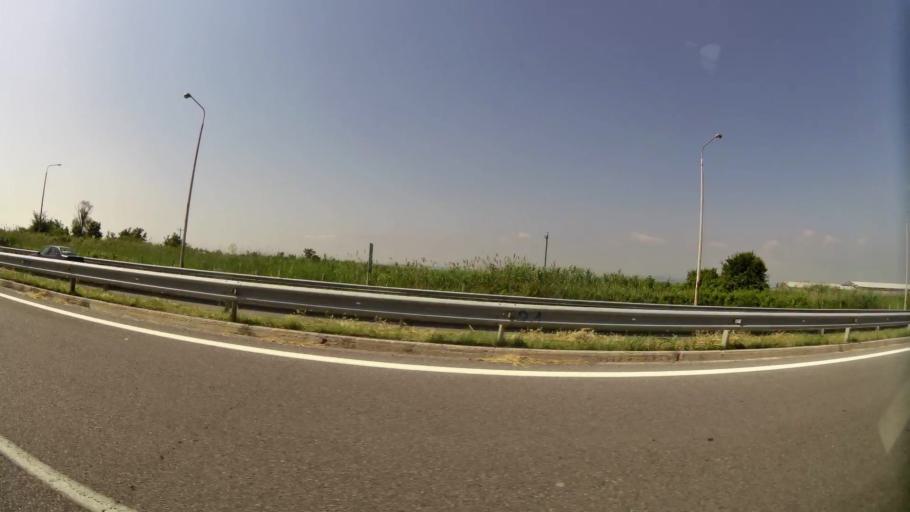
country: GR
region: Central Macedonia
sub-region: Nomos Imathias
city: Kleidi
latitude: 40.5577
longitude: 22.5927
